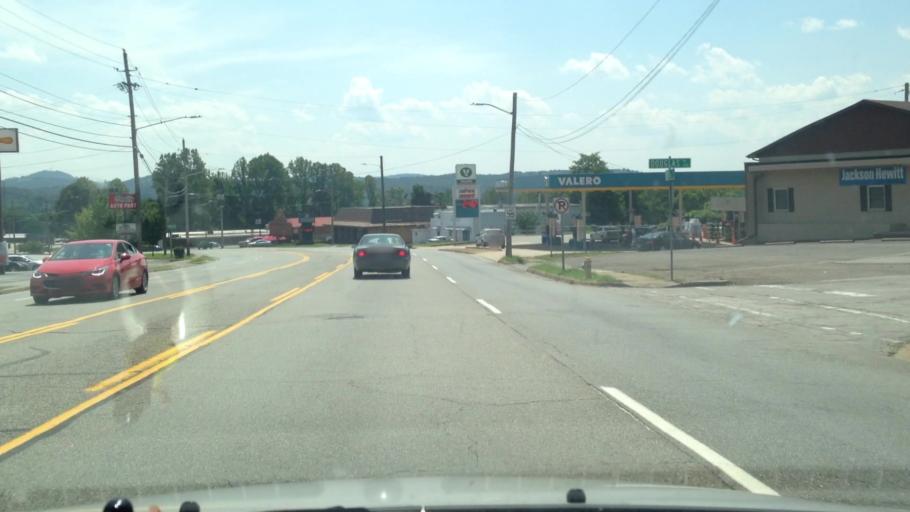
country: US
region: Virginia
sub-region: City of Martinsville
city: Martinsville
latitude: 36.6750
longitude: -79.8771
